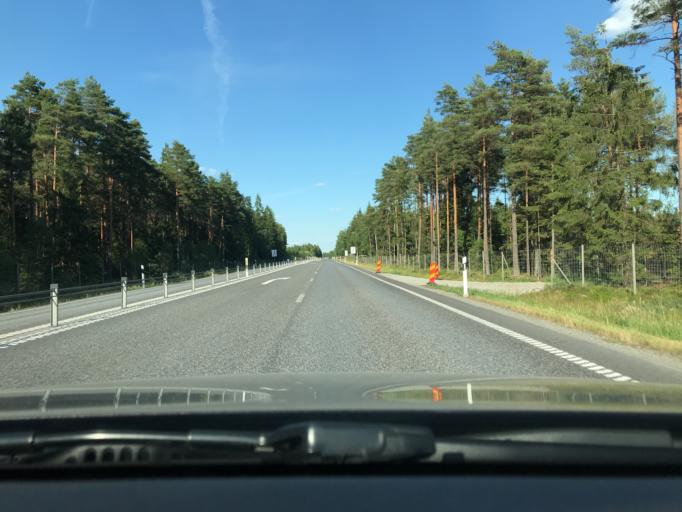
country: SE
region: Kronoberg
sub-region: Alvesta Kommun
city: Vislanda
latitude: 56.7119
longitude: 14.4356
